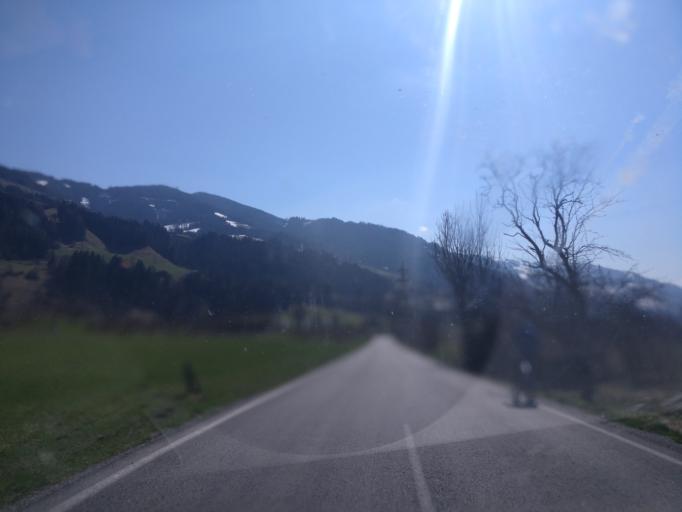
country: AT
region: Salzburg
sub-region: Politischer Bezirk Sankt Johann im Pongau
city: Bischofshofen
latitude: 47.3835
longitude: 13.2155
